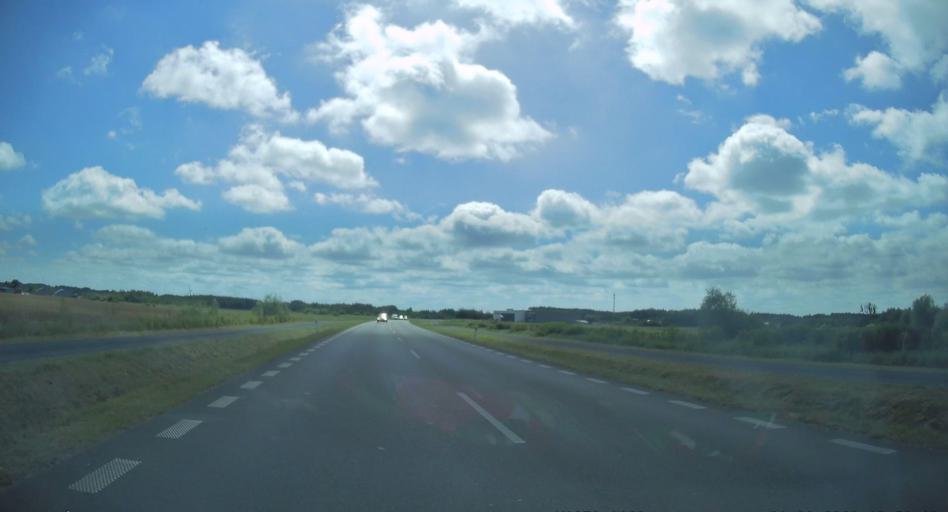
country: PL
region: Subcarpathian Voivodeship
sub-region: Powiat mielecki
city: Padew Narodowa
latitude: 50.3745
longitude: 21.4789
